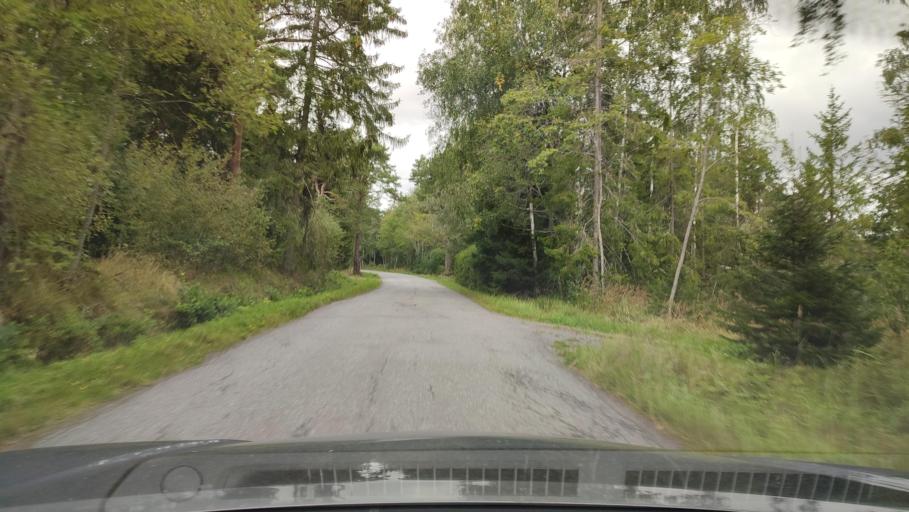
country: FI
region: Ostrobothnia
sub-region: Sydosterbotten
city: Kristinestad
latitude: 62.2547
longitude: 21.3553
